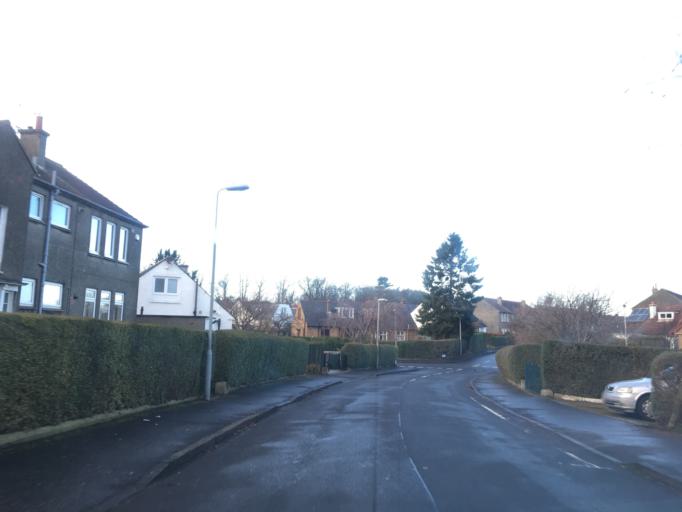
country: GB
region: Scotland
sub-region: Edinburgh
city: Colinton
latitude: 55.9683
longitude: -3.2722
